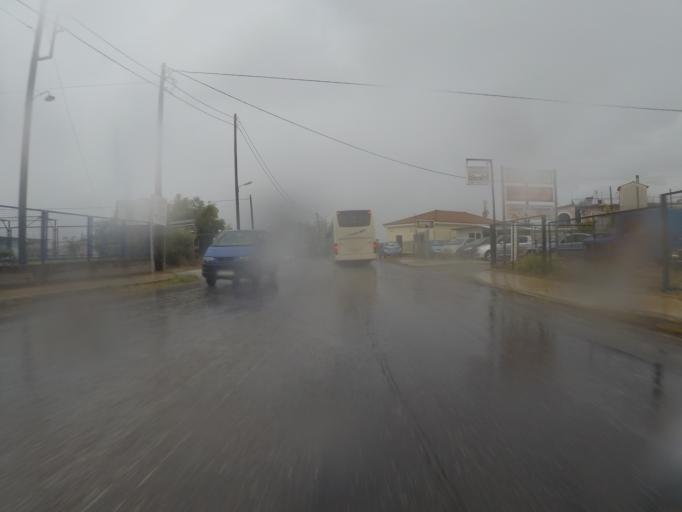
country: GR
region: Peloponnese
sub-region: Nomos Messinias
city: Sperkhoyia
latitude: 37.0473
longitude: 22.0790
